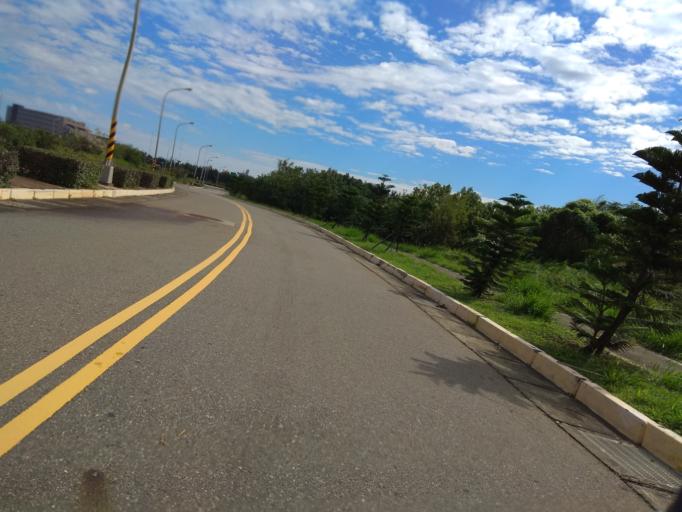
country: TW
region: Taiwan
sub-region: Hsinchu
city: Zhubei
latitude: 25.0448
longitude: 121.0817
